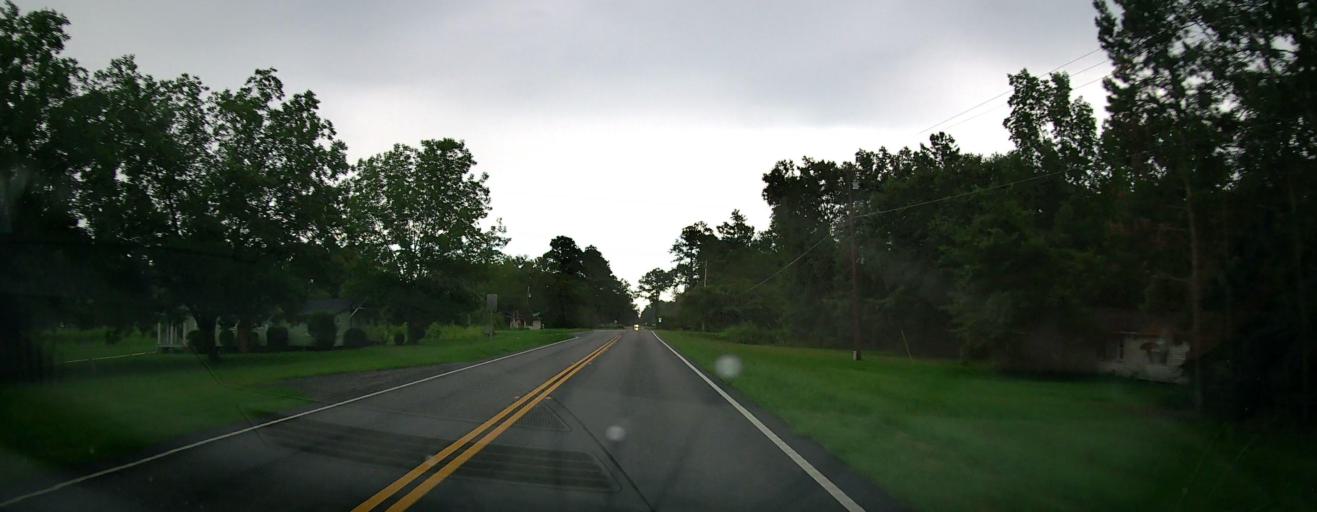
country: US
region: Georgia
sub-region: Glynn County
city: Dock Junction
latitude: 31.2920
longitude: -81.6920
